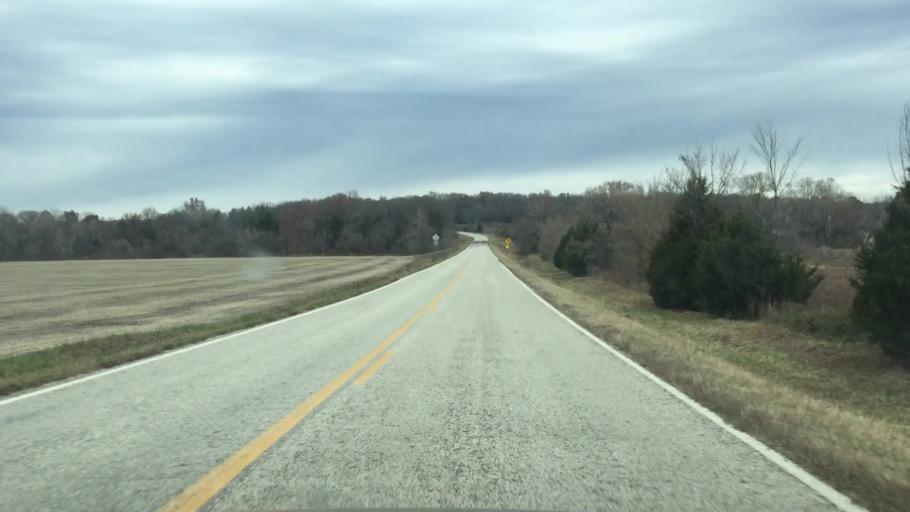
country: US
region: Missouri
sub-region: Saint Clair County
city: Osceola
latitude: 37.9828
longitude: -93.6116
